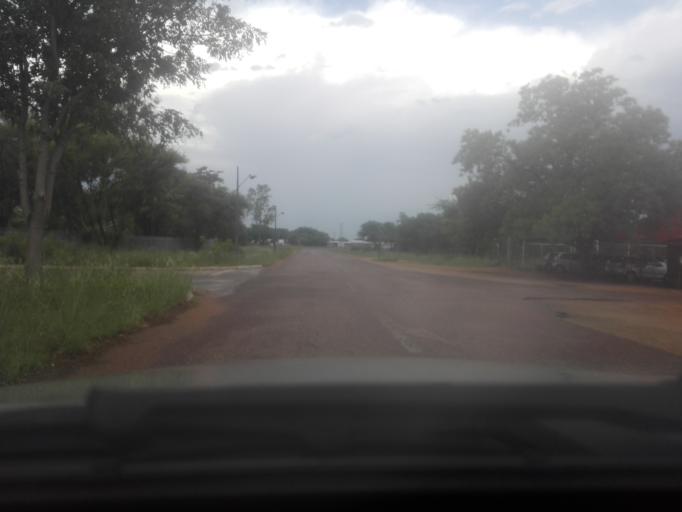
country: BW
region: Kweneng
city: Mmopone
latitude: -24.5580
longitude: 25.9266
